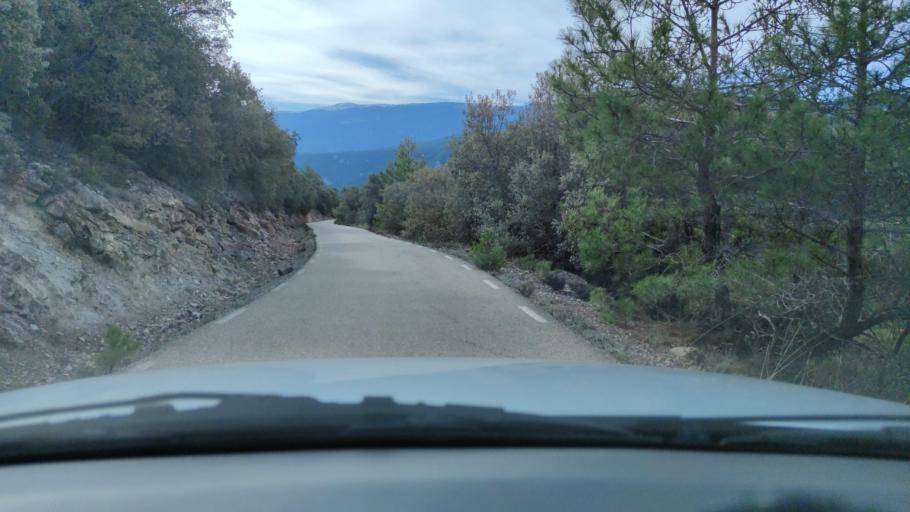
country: ES
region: Catalonia
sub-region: Provincia de Lleida
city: la Seu d'Urgell
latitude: 42.2516
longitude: 1.4110
